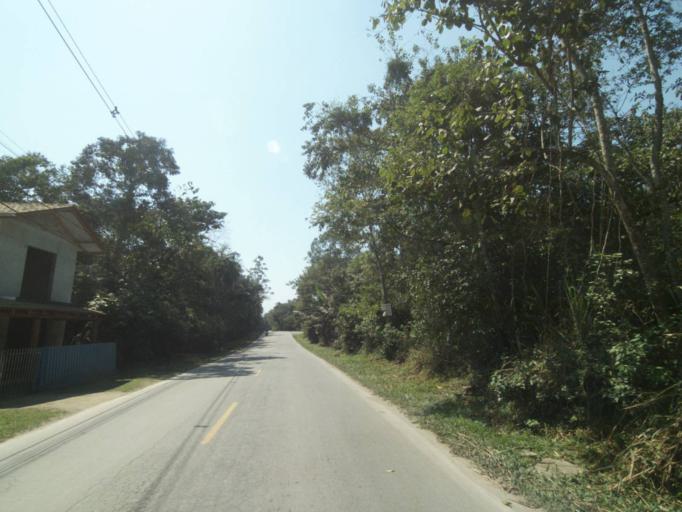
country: BR
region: Parana
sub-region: Paranagua
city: Paranagua
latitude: -25.5642
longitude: -48.6283
